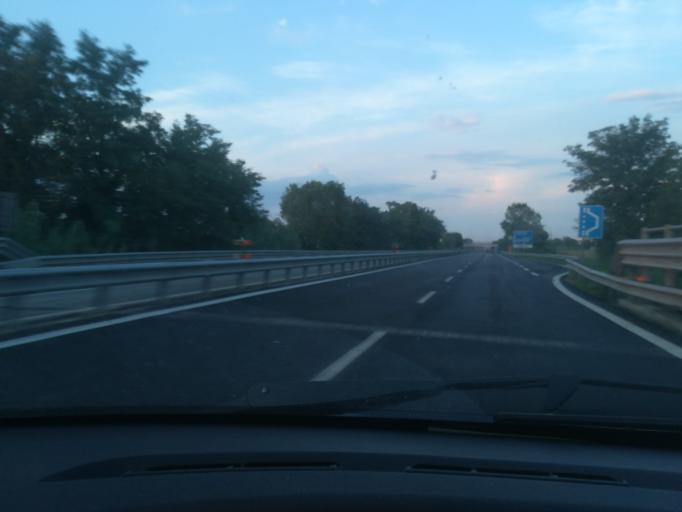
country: IT
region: The Marches
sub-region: Provincia di Macerata
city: Zona Industriale
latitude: 43.2630
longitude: 13.4775
